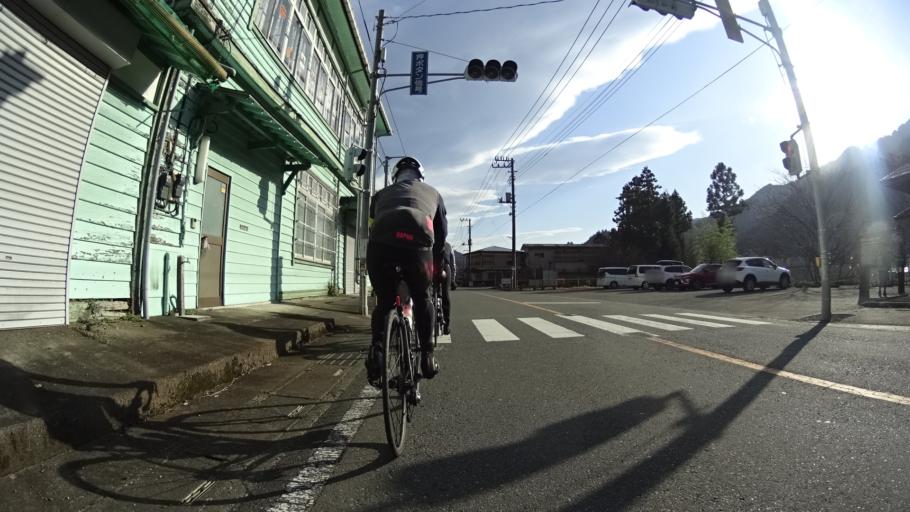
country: JP
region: Tokyo
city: Ome
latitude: 35.8845
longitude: 139.1830
